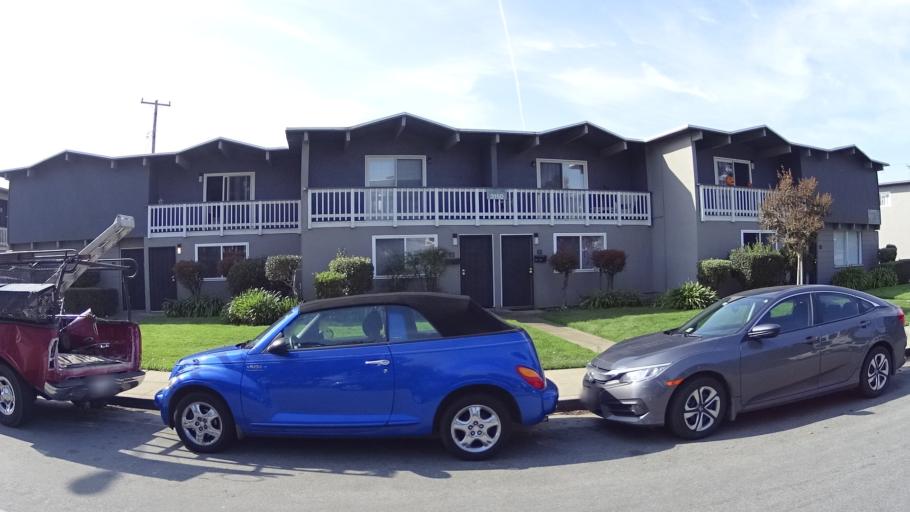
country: US
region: California
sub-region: San Mateo County
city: Foster City
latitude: 37.5427
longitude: -122.2837
